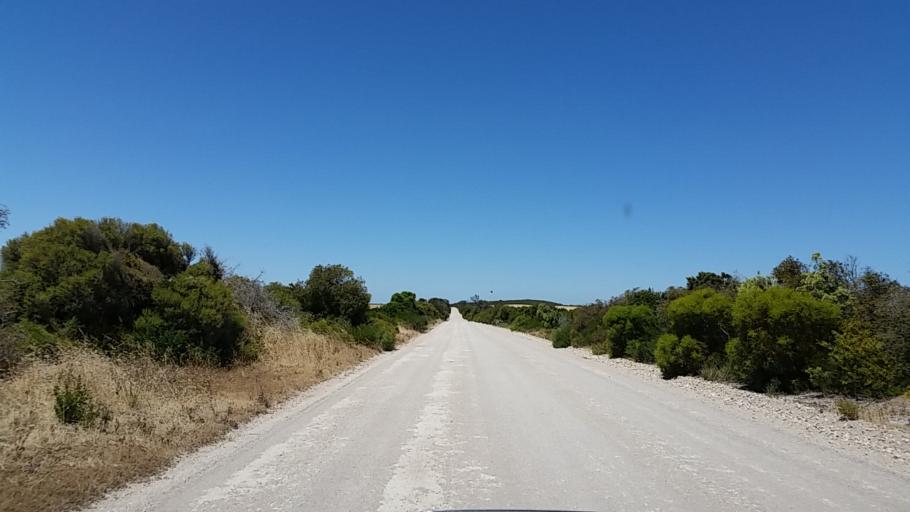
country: AU
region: South Australia
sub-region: Yorke Peninsula
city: Honiton
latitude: -35.0931
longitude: 137.4372
